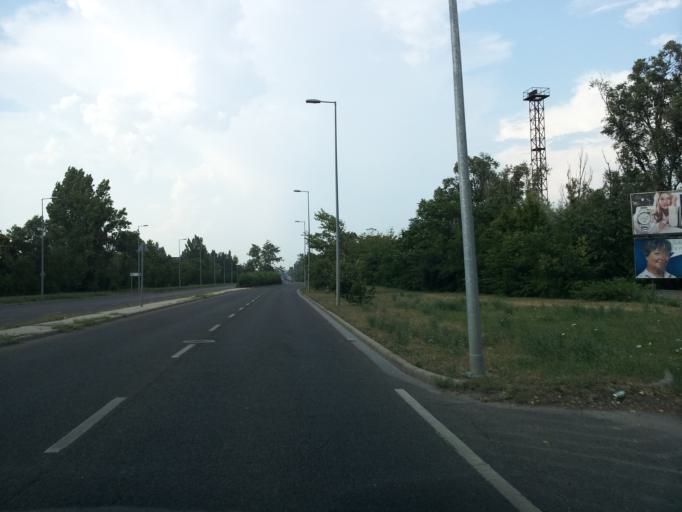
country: HU
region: Budapest
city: Budapest XXII. keruelet
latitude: 47.4512
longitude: 19.0450
